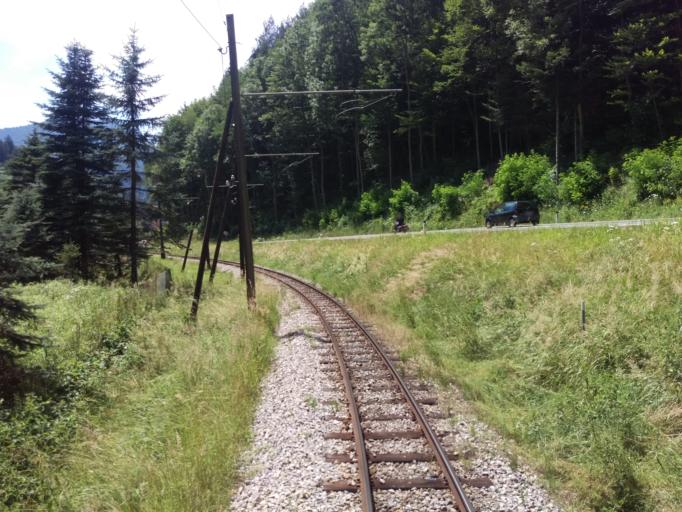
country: AT
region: Styria
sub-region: Politischer Bezirk Bruck-Muerzzuschlag
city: Pernegg an der Mur
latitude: 47.3506
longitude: 15.3652
